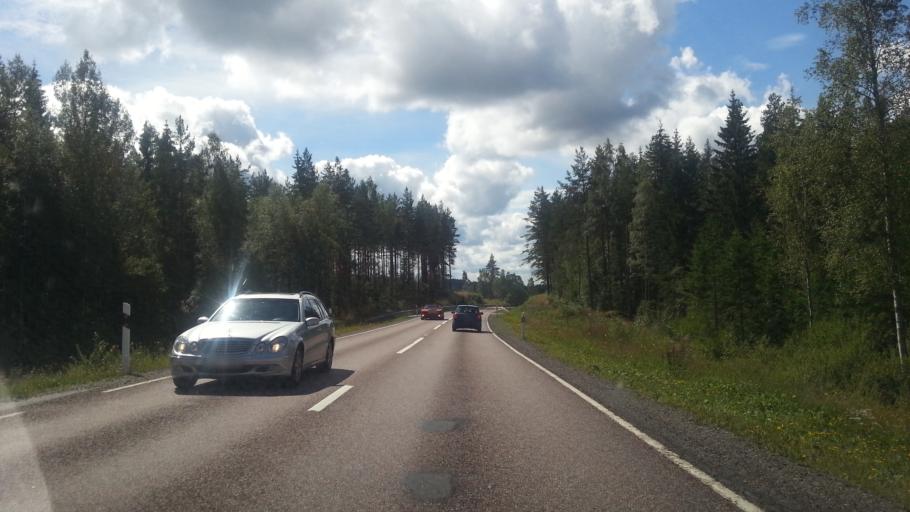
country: SE
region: Dalarna
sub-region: Ludvika Kommun
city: Grangesberg
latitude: 60.0530
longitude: 14.9846
